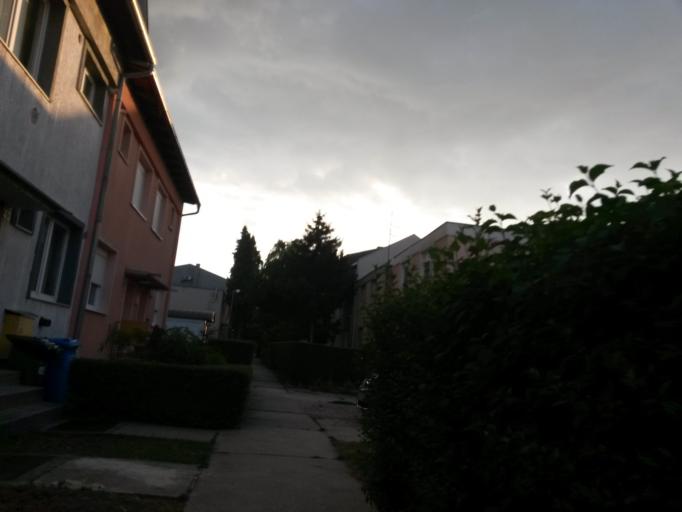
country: HR
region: Osjecko-Baranjska
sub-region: Grad Osijek
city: Osijek
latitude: 45.5426
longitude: 18.7161
